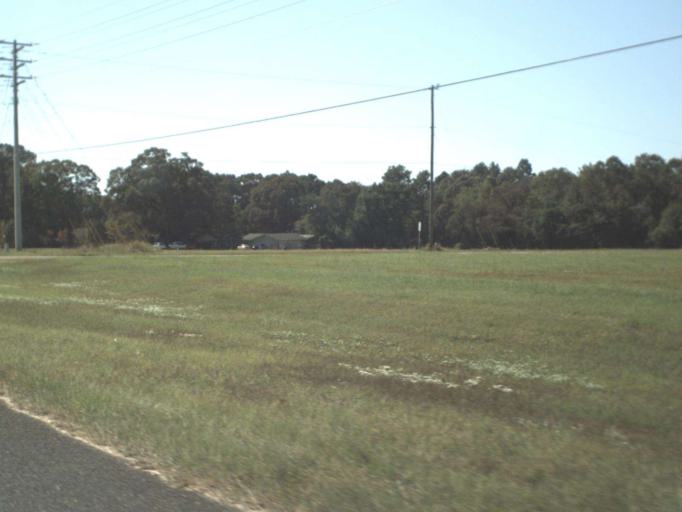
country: US
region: Florida
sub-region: Okaloosa County
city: Crestview
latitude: 30.8159
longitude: -86.5395
